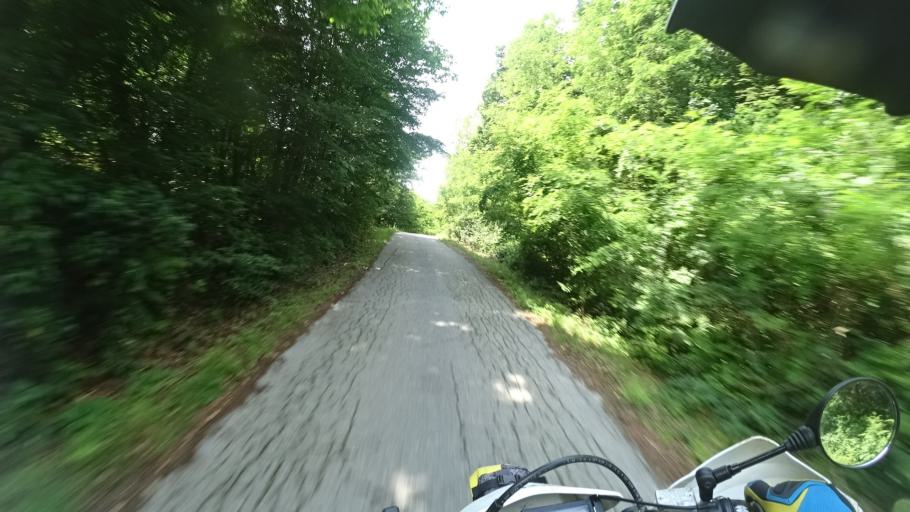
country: HR
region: Sisacko-Moslavacka
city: Gvozd
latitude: 45.4042
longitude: 15.8693
